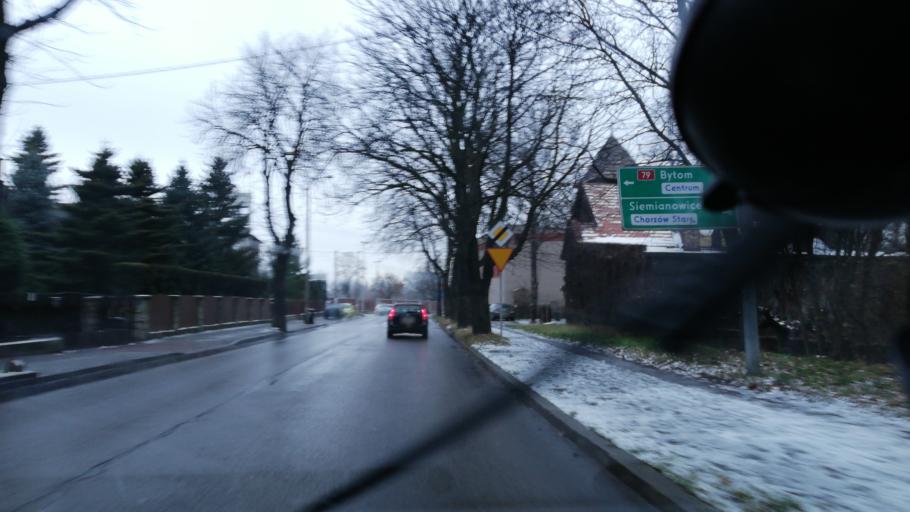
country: PL
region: Silesian Voivodeship
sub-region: Chorzow
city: Chorzow
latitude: 50.2958
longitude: 18.9677
